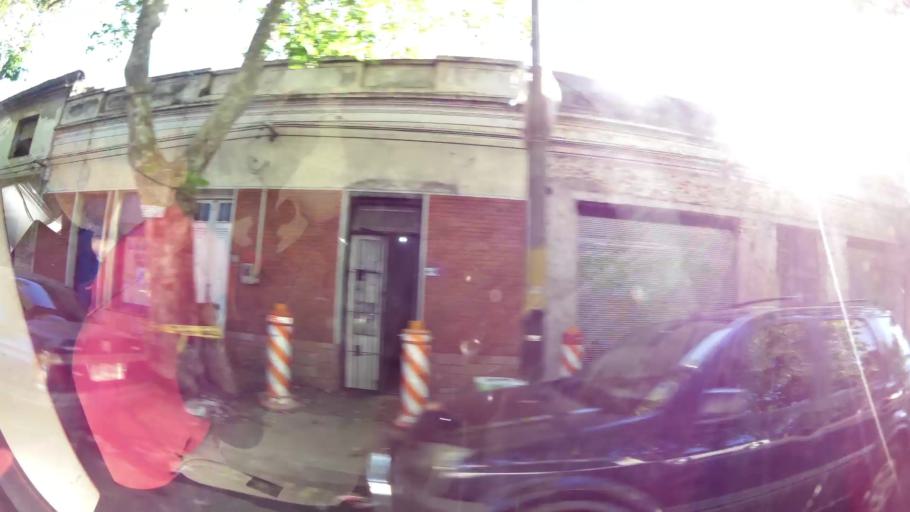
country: UY
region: Canelones
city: La Paz
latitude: -34.8262
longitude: -56.2024
